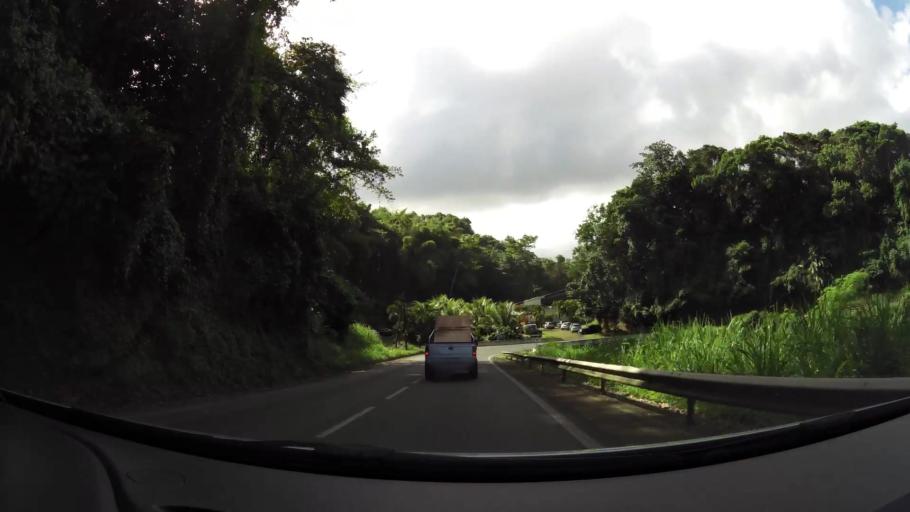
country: MQ
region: Martinique
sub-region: Martinique
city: Le Lorrain
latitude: 14.8348
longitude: -61.0749
